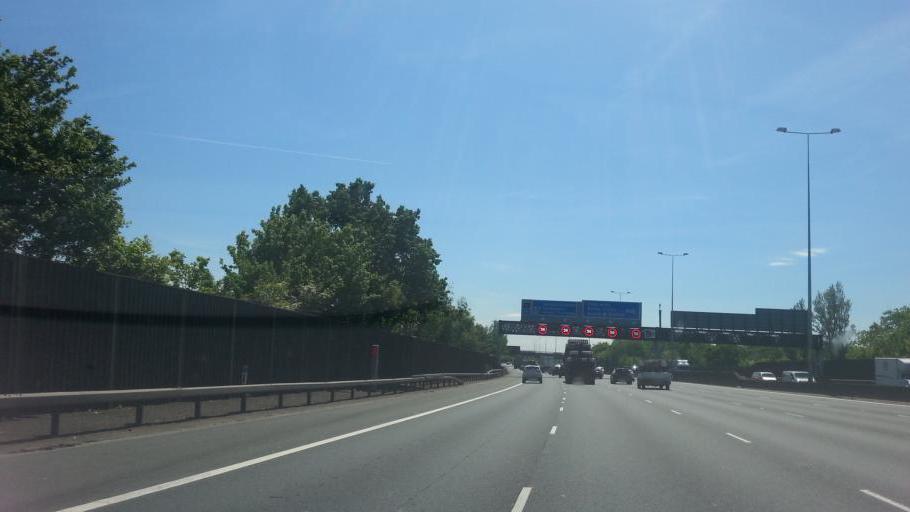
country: GB
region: England
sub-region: Surrey
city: Egham
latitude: 51.4269
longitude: -0.5407
